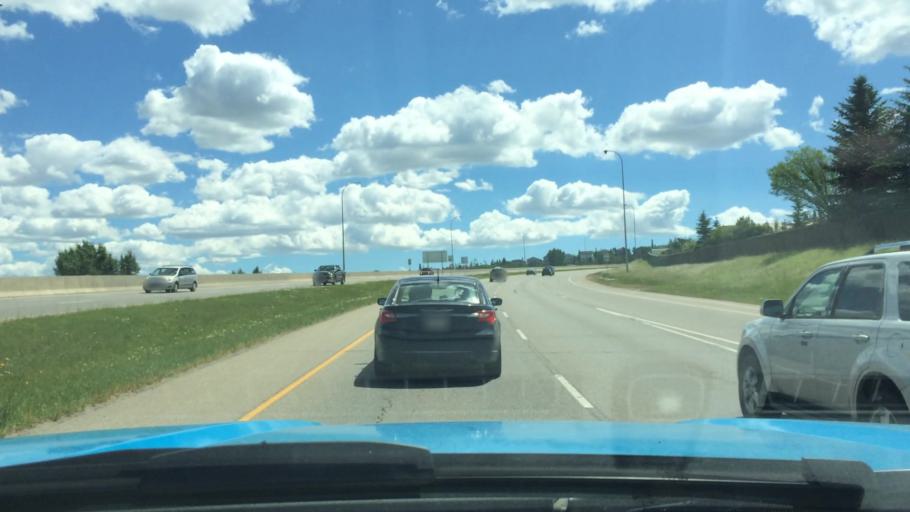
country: CA
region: Alberta
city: Calgary
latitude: 51.1400
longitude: -114.1216
